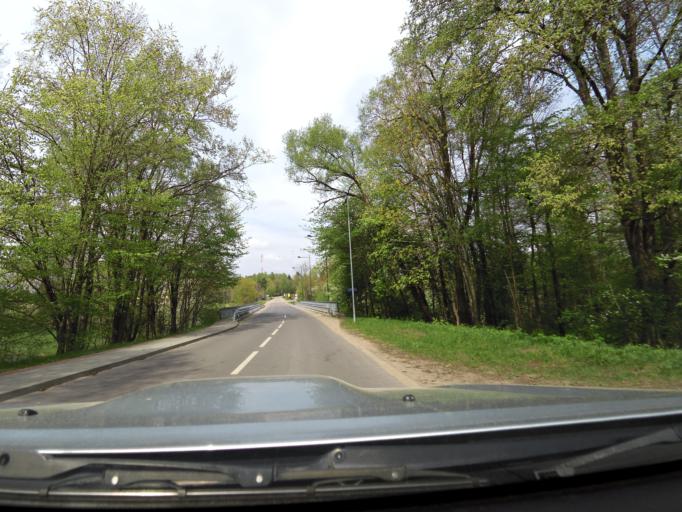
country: LT
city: Salcininkai
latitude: 54.4340
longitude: 25.3001
